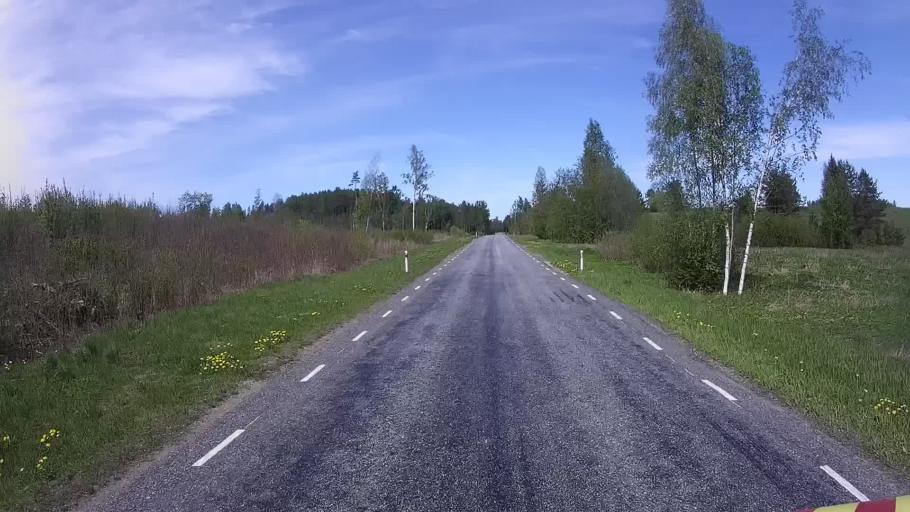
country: EE
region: Valgamaa
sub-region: Valga linn
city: Valga
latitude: 57.6714
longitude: 26.2844
